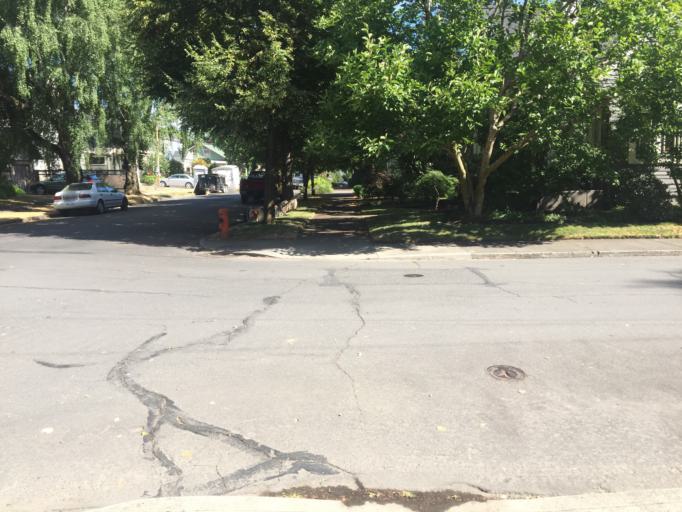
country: US
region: Oregon
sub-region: Multnomah County
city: Portland
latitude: 45.5400
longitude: -122.6332
